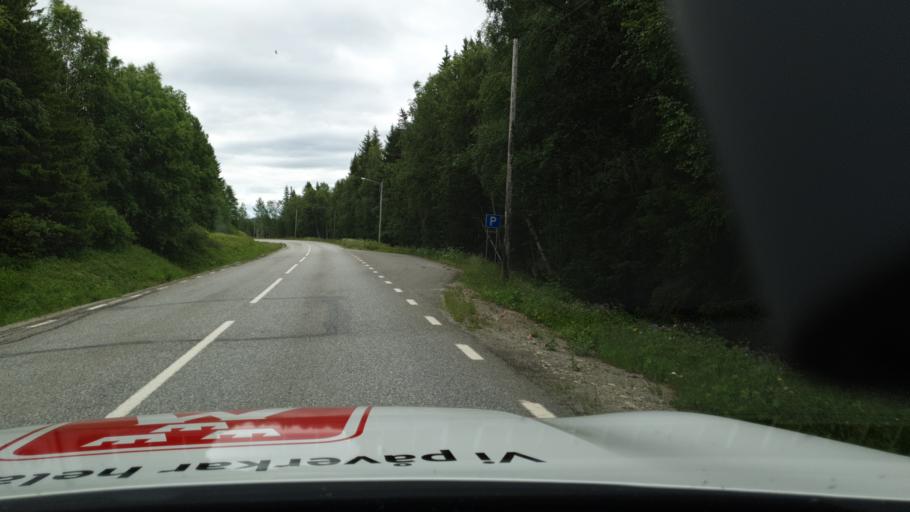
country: SE
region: Vaesterbotten
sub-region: Lycksele Kommun
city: Soderfors
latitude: 64.6483
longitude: 17.8512
